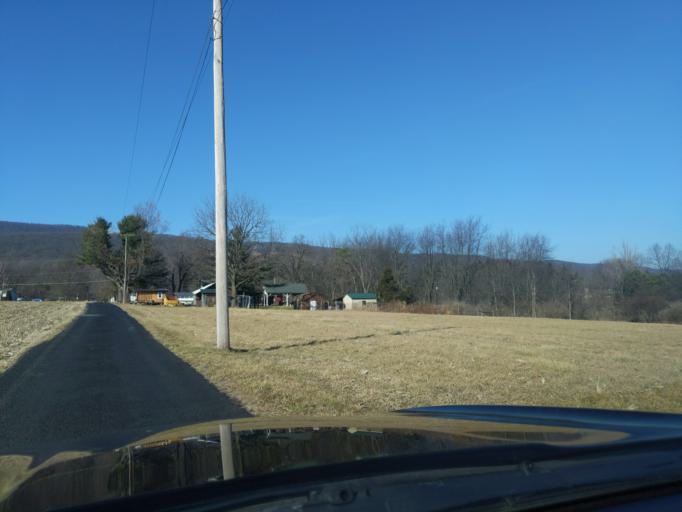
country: US
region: Pennsylvania
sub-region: Blair County
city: Bellwood
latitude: 40.5604
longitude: -78.2754
